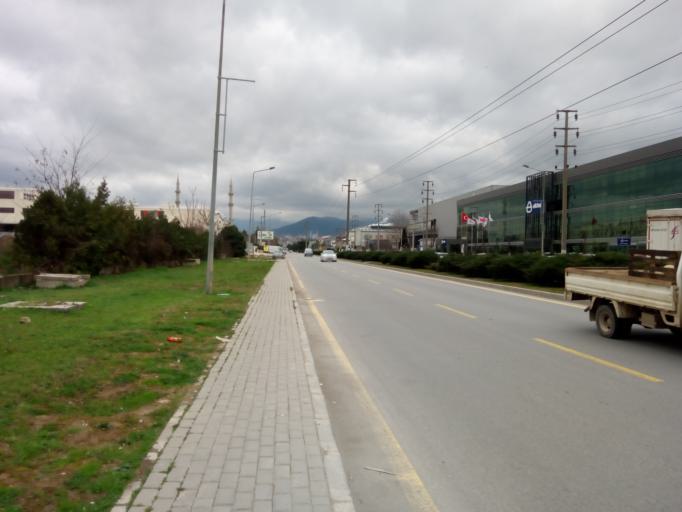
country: TR
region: Bursa
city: Niluefer
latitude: 40.2452
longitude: 28.9590
